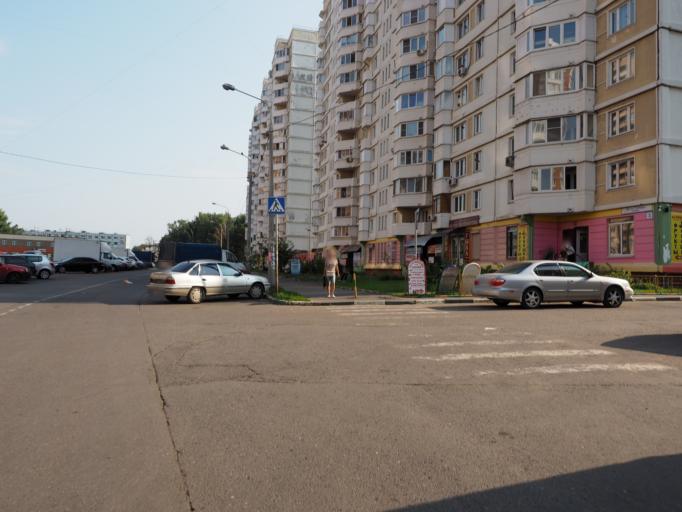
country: RU
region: Moskovskaya
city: Oktyabr'skiy
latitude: 55.6062
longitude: 37.9681
